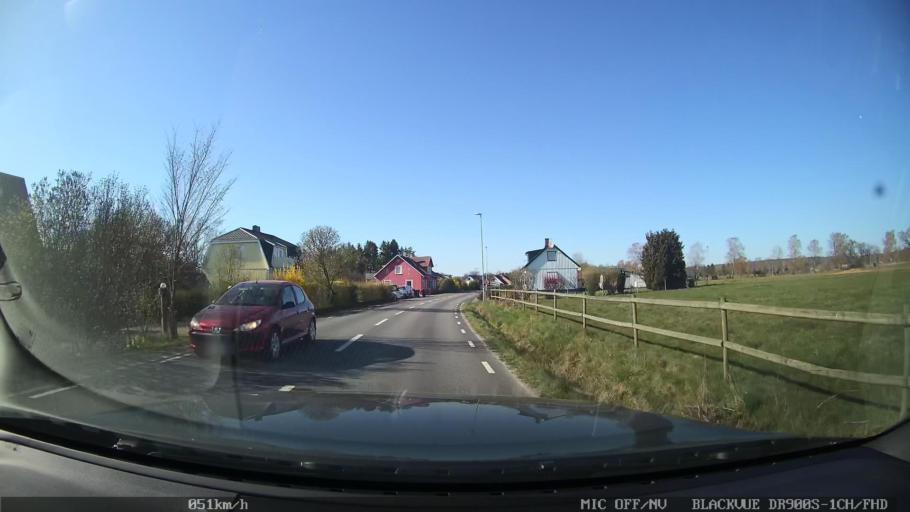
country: SE
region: Skane
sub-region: Bjuvs Kommun
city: Billesholm
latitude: 56.0512
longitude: 12.9985
